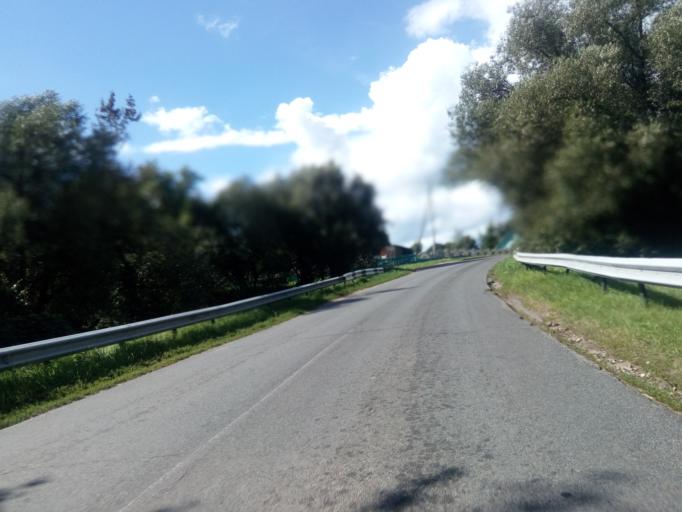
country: BY
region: Vitebsk
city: Dzisna
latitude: 55.7025
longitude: 28.1852
